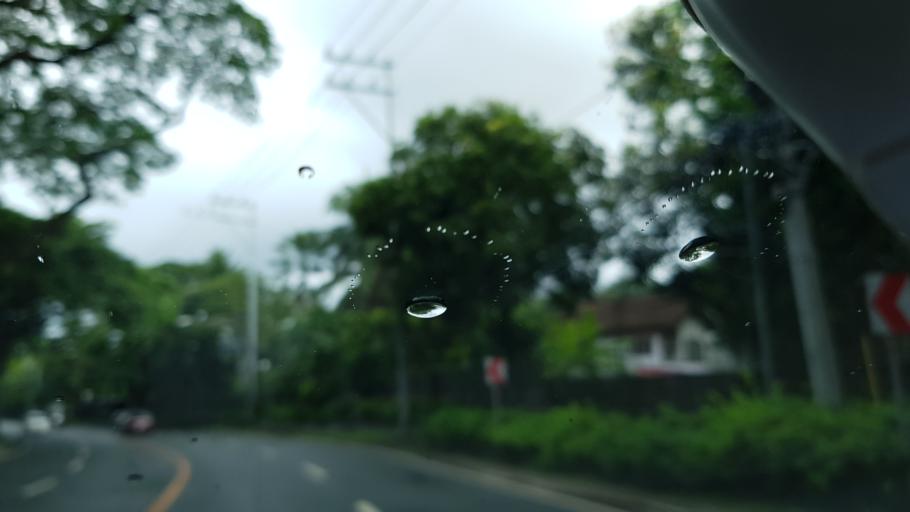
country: PH
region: Metro Manila
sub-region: Makati City
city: Makati City
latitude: 14.5477
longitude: 121.0407
